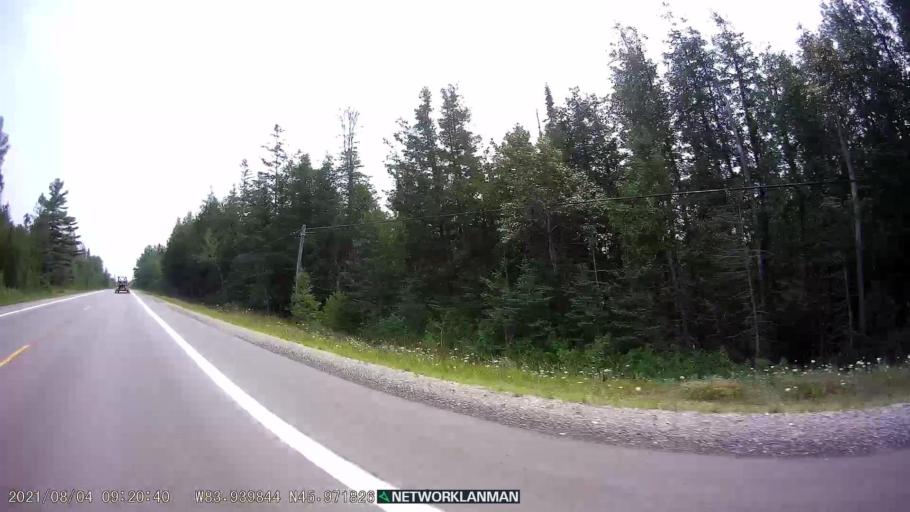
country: CA
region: Ontario
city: Thessalon
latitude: 45.9724
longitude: -83.9381
